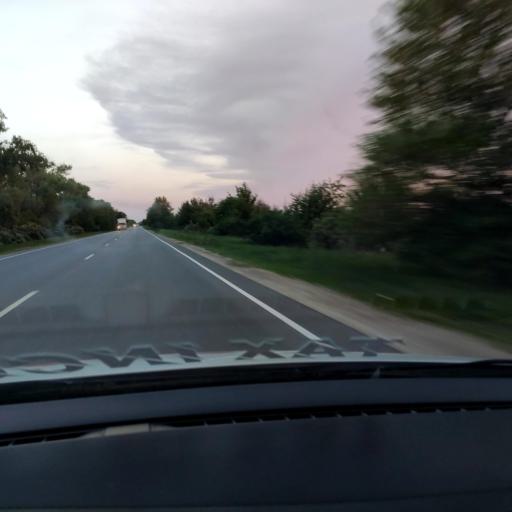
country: RU
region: Voronezj
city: Novovoronezh
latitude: 51.4178
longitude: 39.3000
